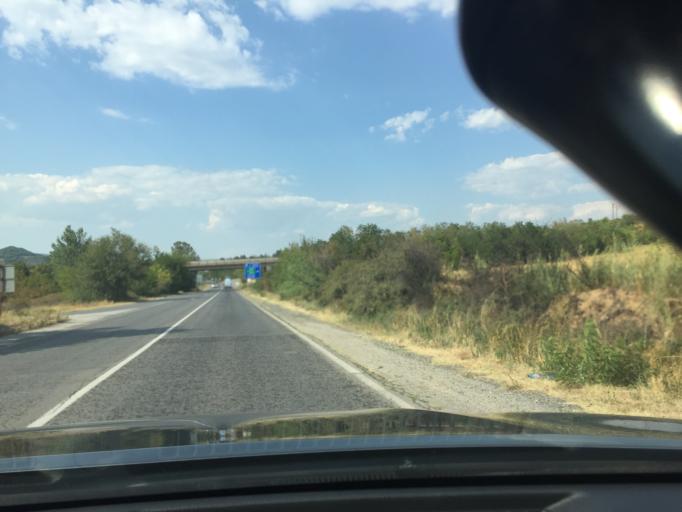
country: BG
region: Kyustendil
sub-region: Obshtina Boboshevo
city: Boboshevo
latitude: 42.1526
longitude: 23.0408
